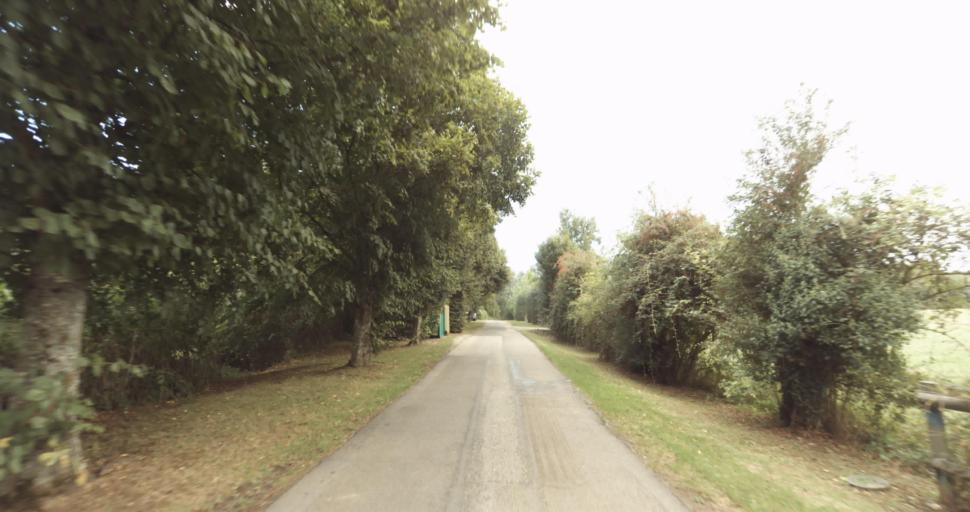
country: FR
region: Lower Normandy
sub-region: Departement de l'Orne
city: Gace
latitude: 48.7737
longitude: 0.3417
